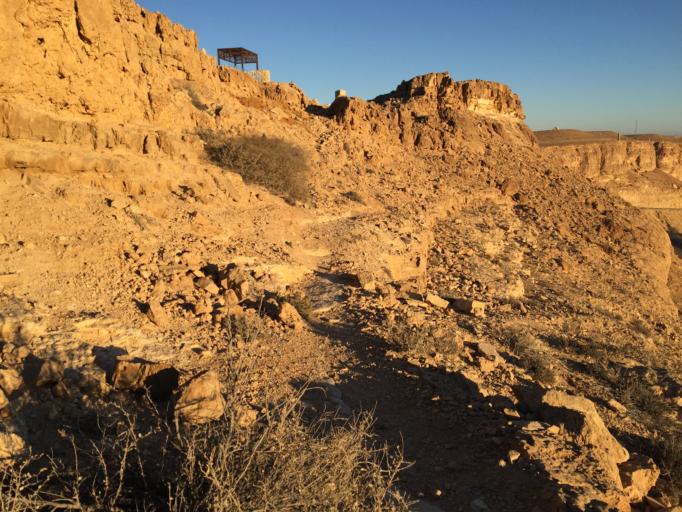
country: IL
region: Southern District
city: Mitzpe Ramon
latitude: 30.6118
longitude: 34.8083
